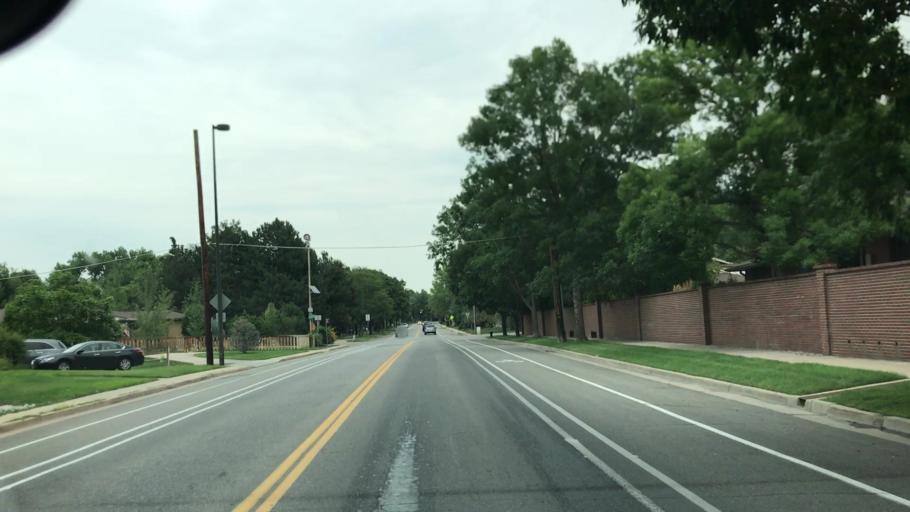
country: US
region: Colorado
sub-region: Arapahoe County
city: Cherry Hills Village
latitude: 39.6676
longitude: -104.9563
